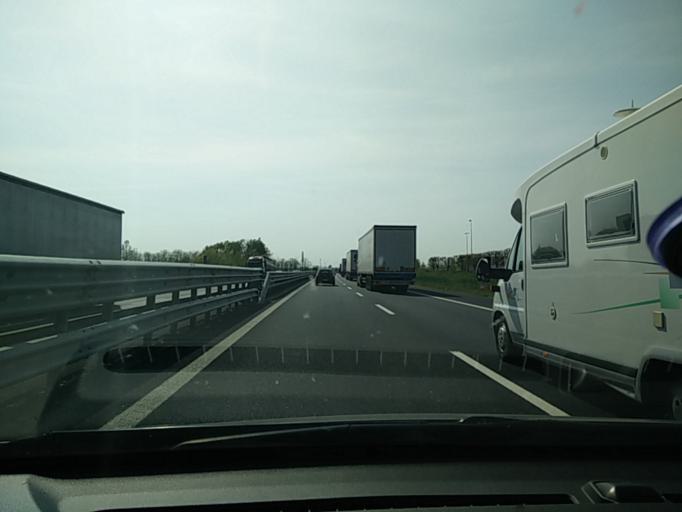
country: IT
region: Veneto
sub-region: Provincia di Venezia
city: Summaga
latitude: 45.7900
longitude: 12.8162
